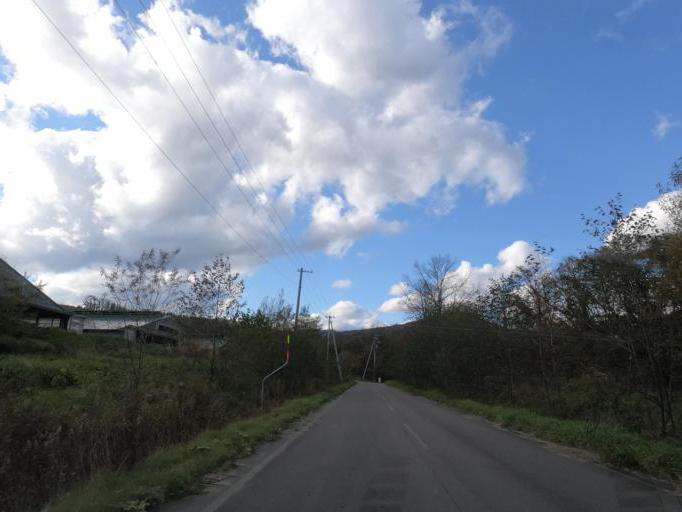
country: JP
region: Hokkaido
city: Otofuke
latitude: 43.2903
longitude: 143.2279
